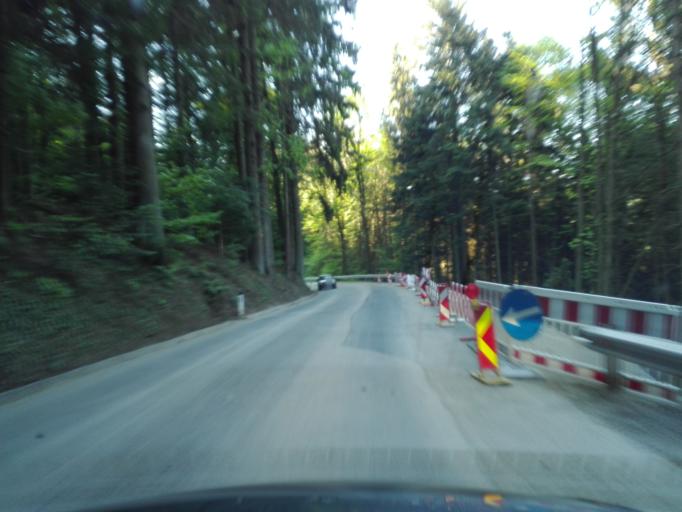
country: DE
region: Bavaria
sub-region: Lower Bavaria
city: Obernzell
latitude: 48.5348
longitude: 13.6500
